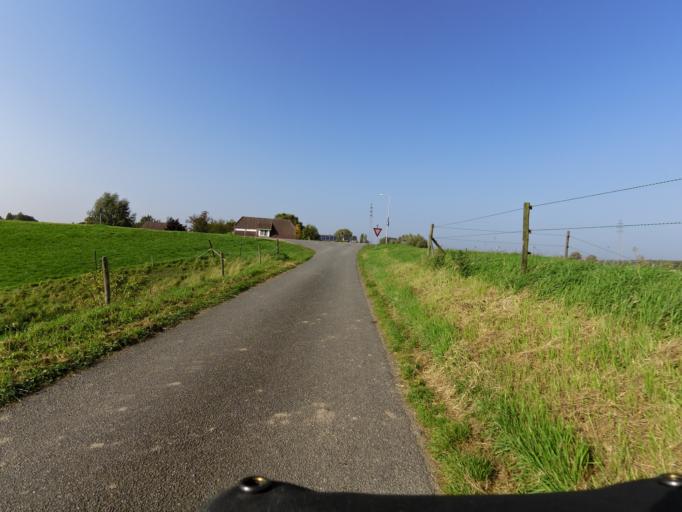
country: NL
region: Gelderland
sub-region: Gemeente Duiven
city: Duiven
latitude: 51.9031
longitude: 6.0037
